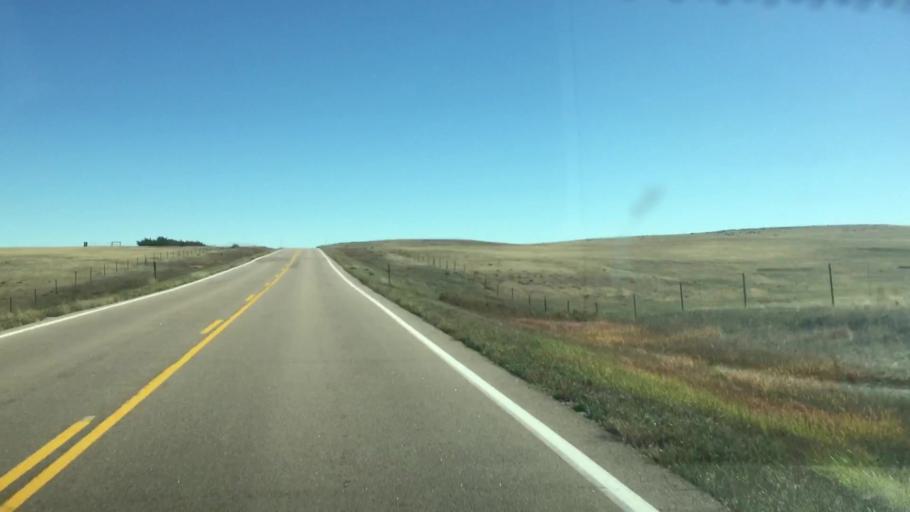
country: US
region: Colorado
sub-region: Lincoln County
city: Limon
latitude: 39.2822
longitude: -103.9884
